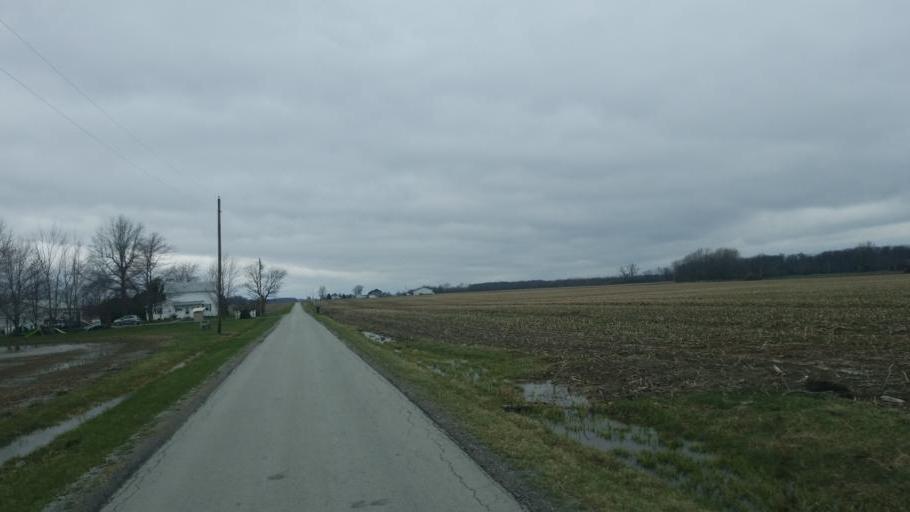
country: US
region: Ohio
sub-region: Hardin County
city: Forest
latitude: 40.7236
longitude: -83.4710
